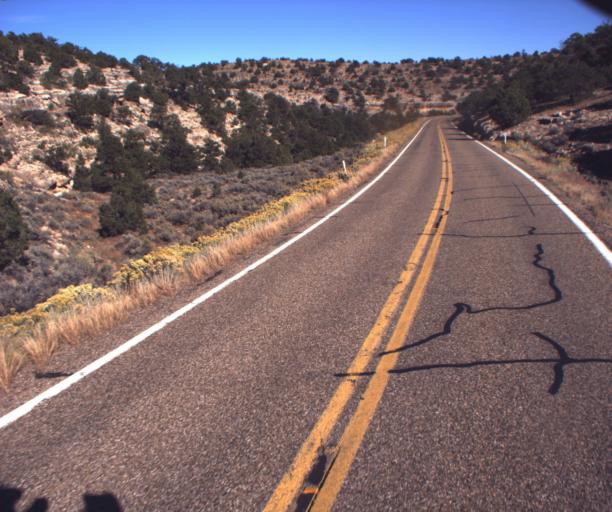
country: US
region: Arizona
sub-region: Coconino County
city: Fredonia
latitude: 36.7292
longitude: -112.0900
